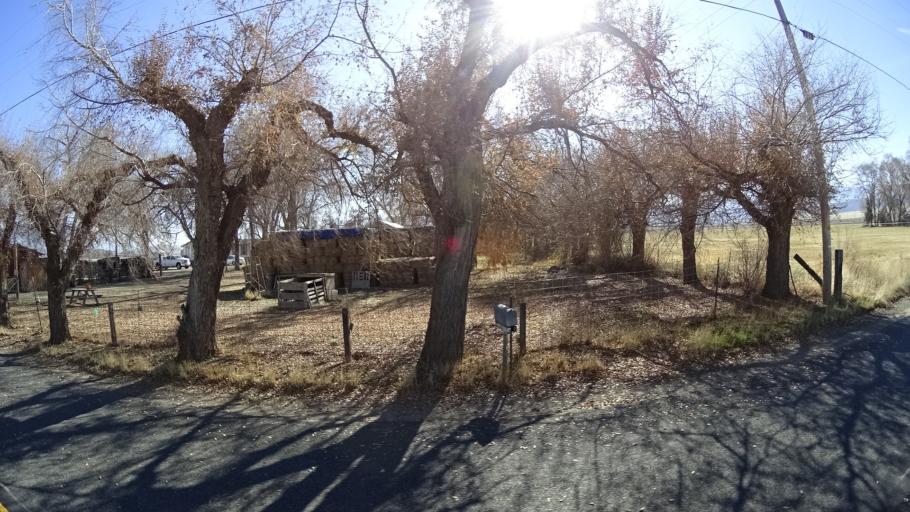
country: US
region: California
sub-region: Siskiyou County
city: Montague
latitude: 41.5747
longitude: -122.5370
